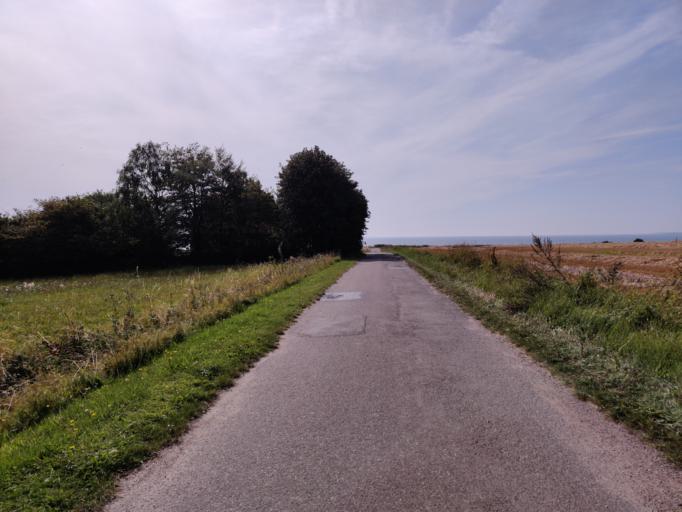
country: DK
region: Zealand
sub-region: Guldborgsund Kommune
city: Nykobing Falster
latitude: 54.6325
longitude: 11.8923
